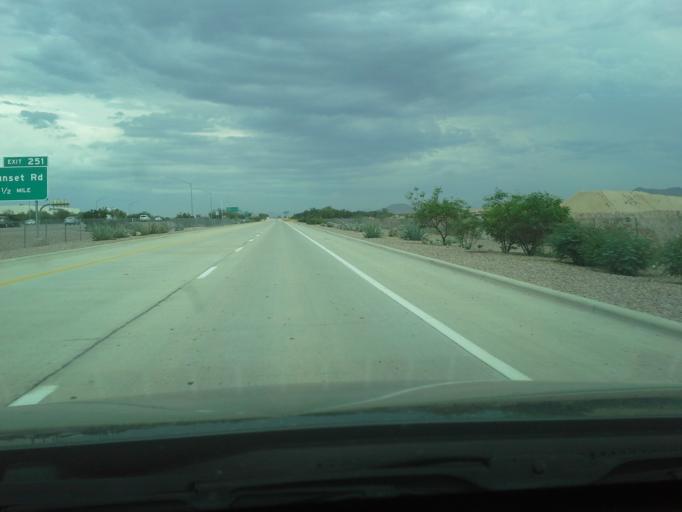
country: US
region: Arizona
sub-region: Pima County
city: Flowing Wells
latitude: 32.3192
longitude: -111.0494
